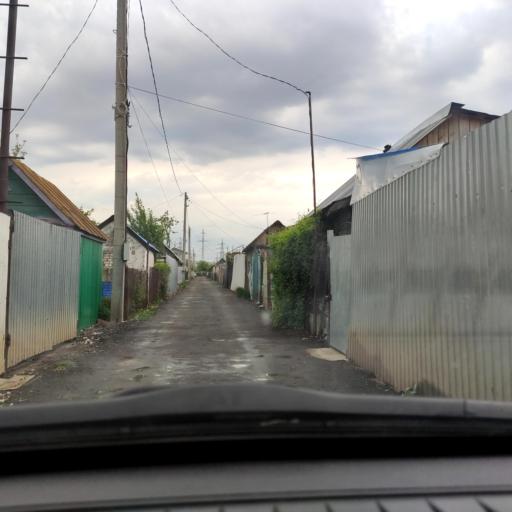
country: RU
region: Samara
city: Tol'yatti
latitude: 53.5436
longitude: 49.4391
